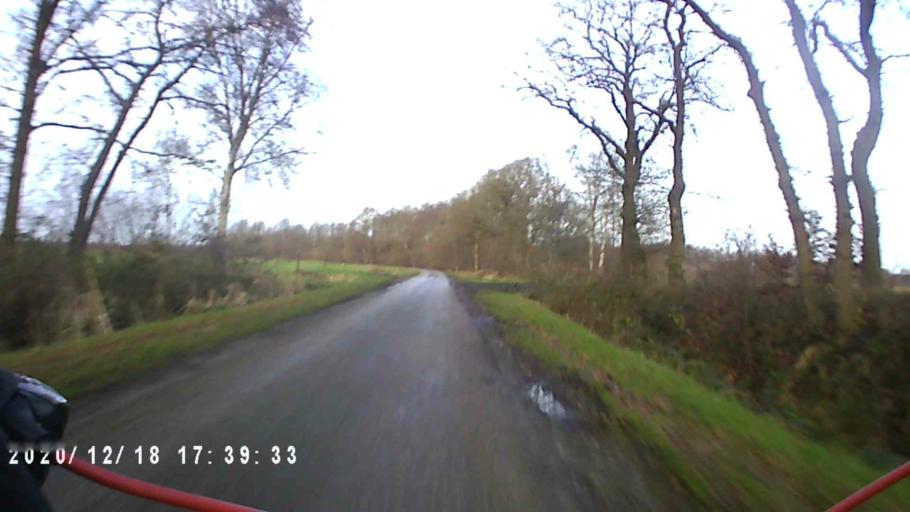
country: NL
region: Drenthe
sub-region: Gemeente Tynaarlo
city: Vries
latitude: 53.0912
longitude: 6.5806
